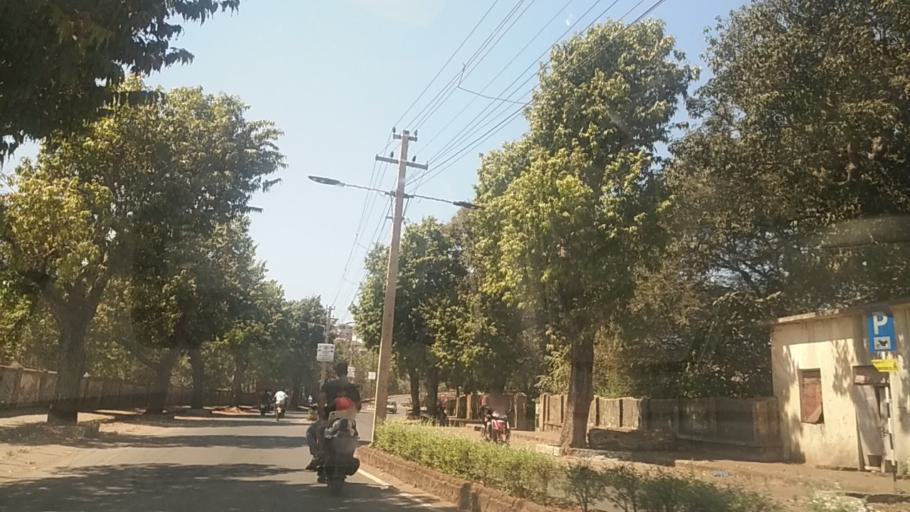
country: IN
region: Goa
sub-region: South Goa
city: Vasco Da Gama
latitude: 15.3963
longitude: 73.8071
